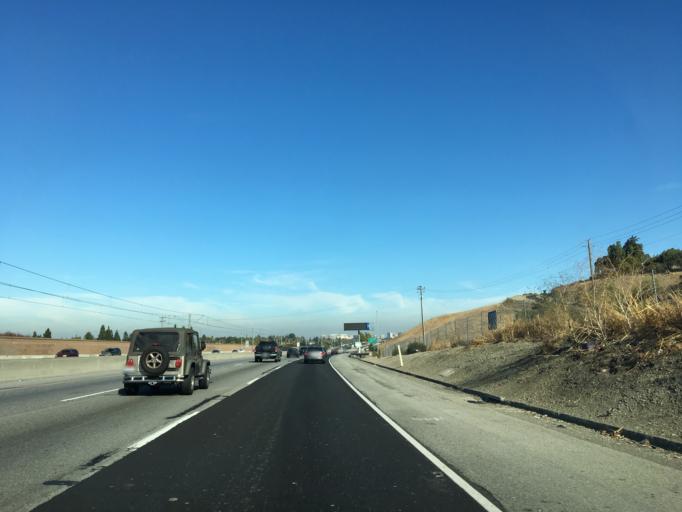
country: US
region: California
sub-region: Santa Clara County
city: Seven Trees
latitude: 37.2881
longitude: -121.8698
